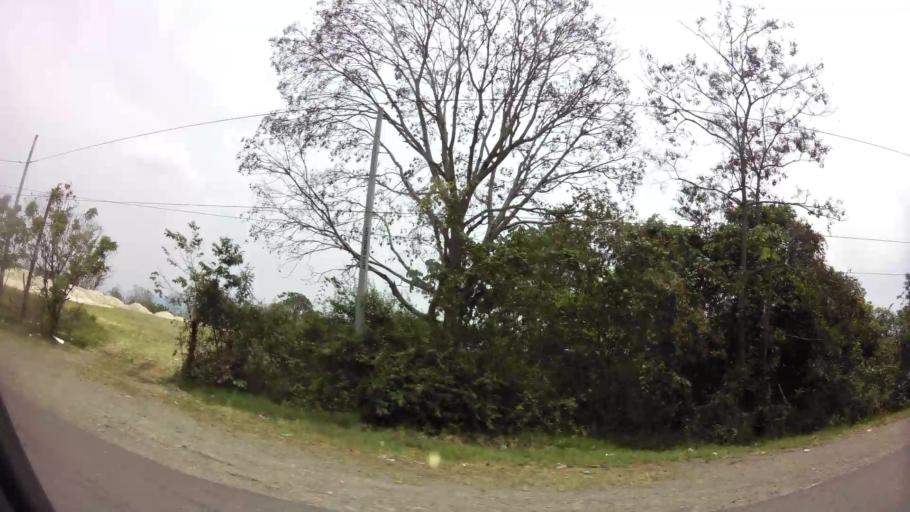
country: HN
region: Comayagua
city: Taulabe
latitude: 14.6767
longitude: -87.9557
